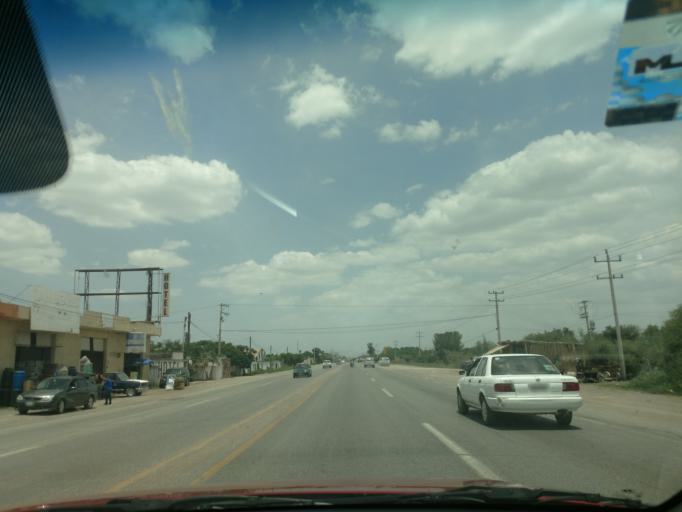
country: MX
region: San Luis Potosi
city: Ciudad Fernandez
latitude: 21.9397
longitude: -100.0365
